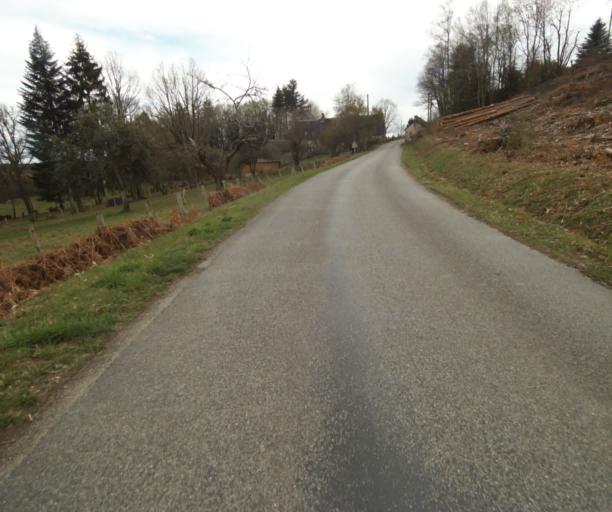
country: FR
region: Limousin
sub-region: Departement de la Correze
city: Argentat
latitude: 45.1914
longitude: 1.9576
